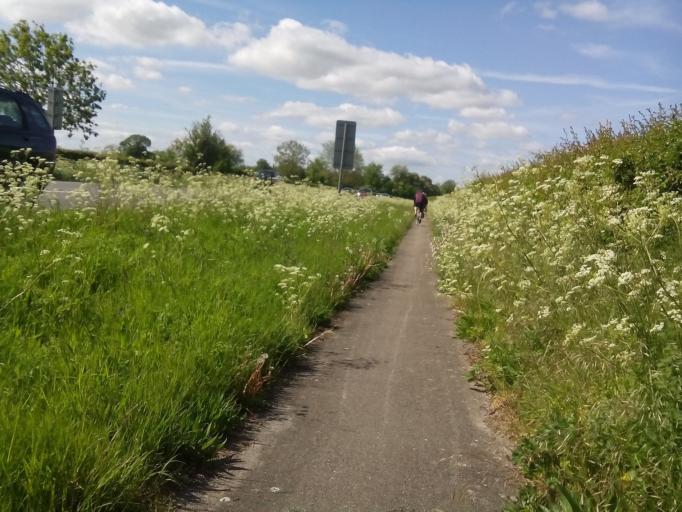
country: GB
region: England
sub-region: Cambridgeshire
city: Harston
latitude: 52.1325
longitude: 0.0720
